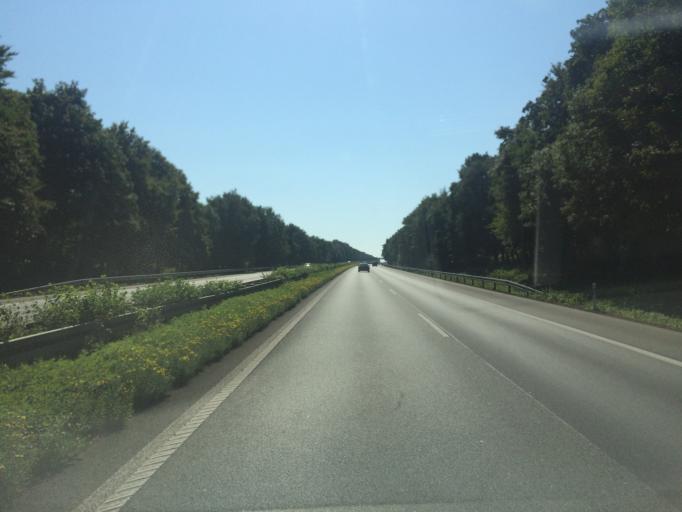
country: DE
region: North Rhine-Westphalia
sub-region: Regierungsbezirk Munster
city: Ascheberg
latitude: 51.7446
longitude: 7.6489
